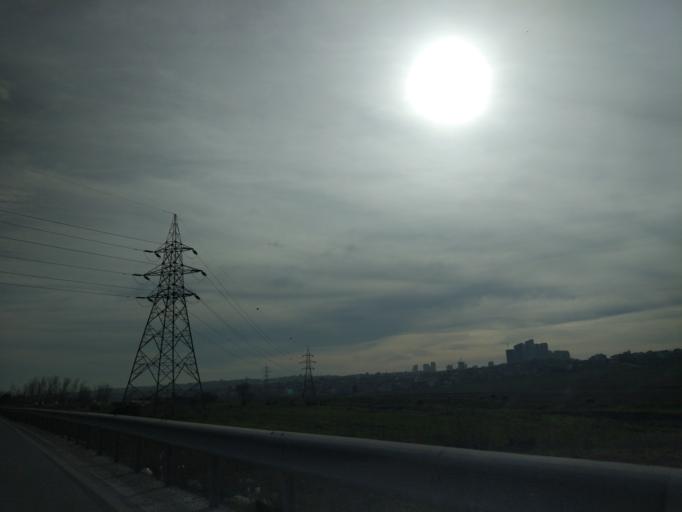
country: TR
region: Istanbul
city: Esenyurt
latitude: 41.0566
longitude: 28.7010
